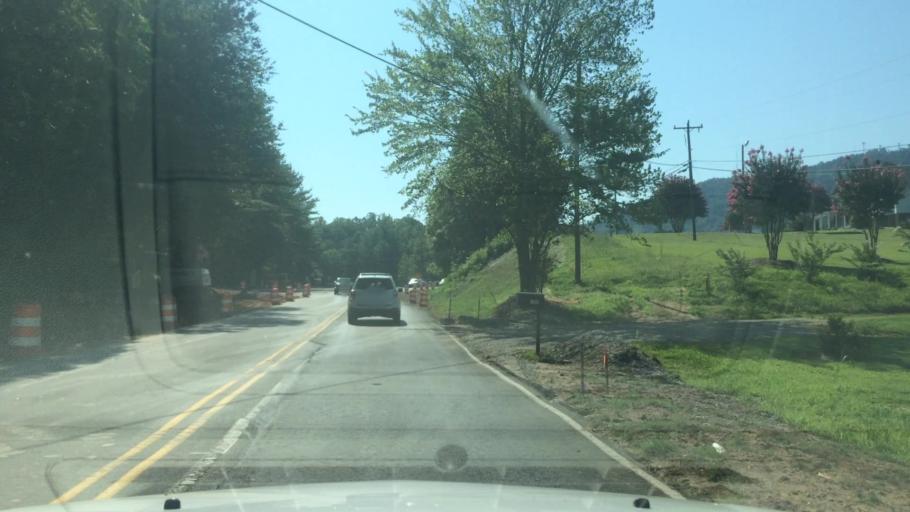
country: US
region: North Carolina
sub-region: Caldwell County
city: Lenoir
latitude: 35.9223
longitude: -81.5011
